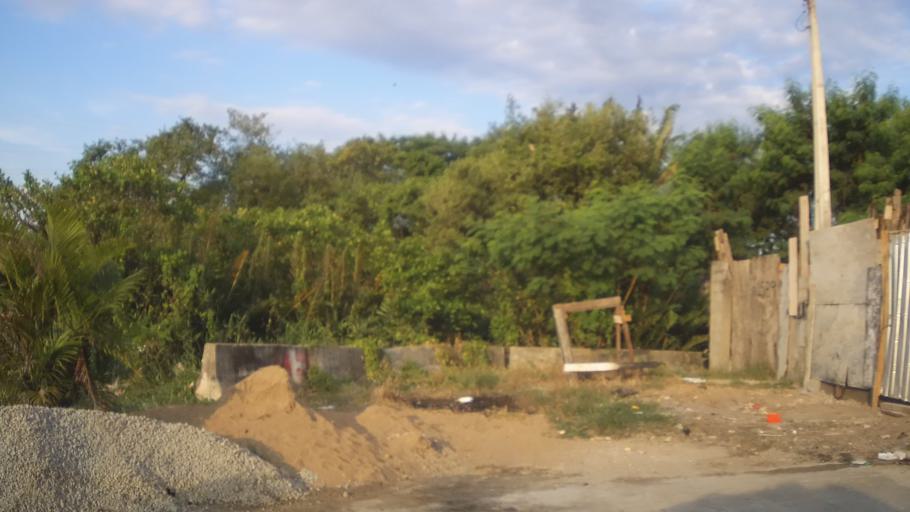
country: BR
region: Sao Paulo
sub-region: Praia Grande
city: Praia Grande
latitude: -23.9949
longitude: -46.4294
